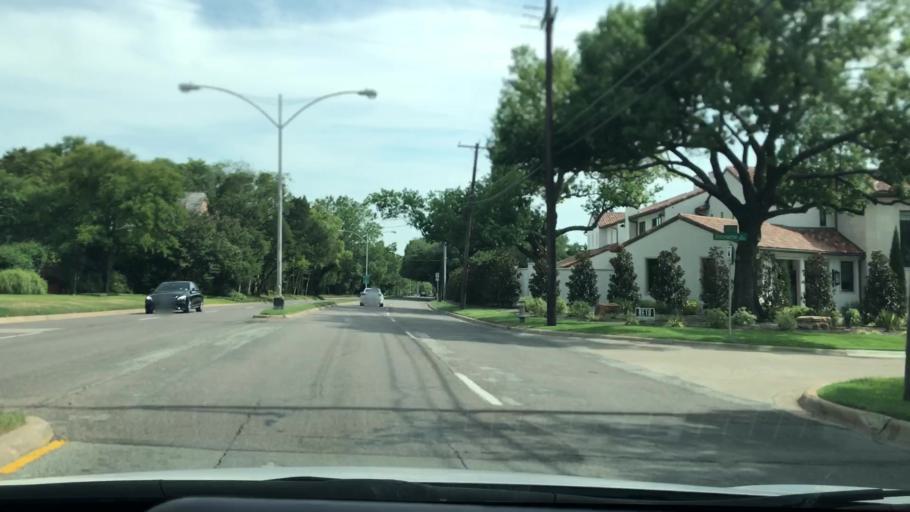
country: US
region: Texas
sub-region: Dallas County
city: University Park
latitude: 32.8710
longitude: -96.8213
